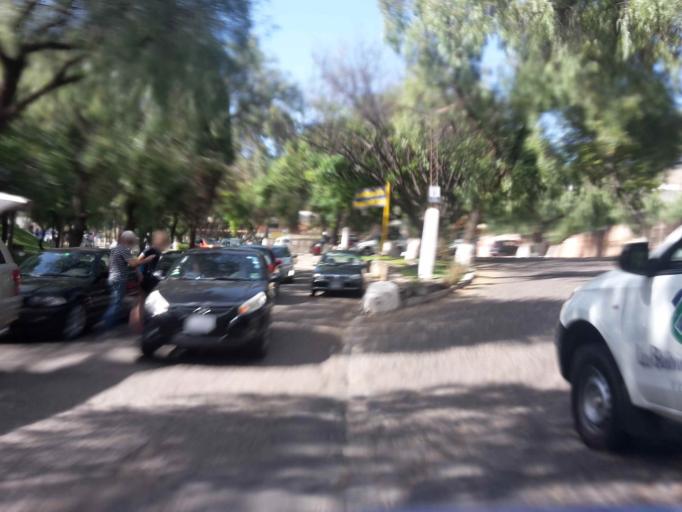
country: BO
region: Cochabamba
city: Cochabamba
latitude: -17.3718
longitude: -66.1318
